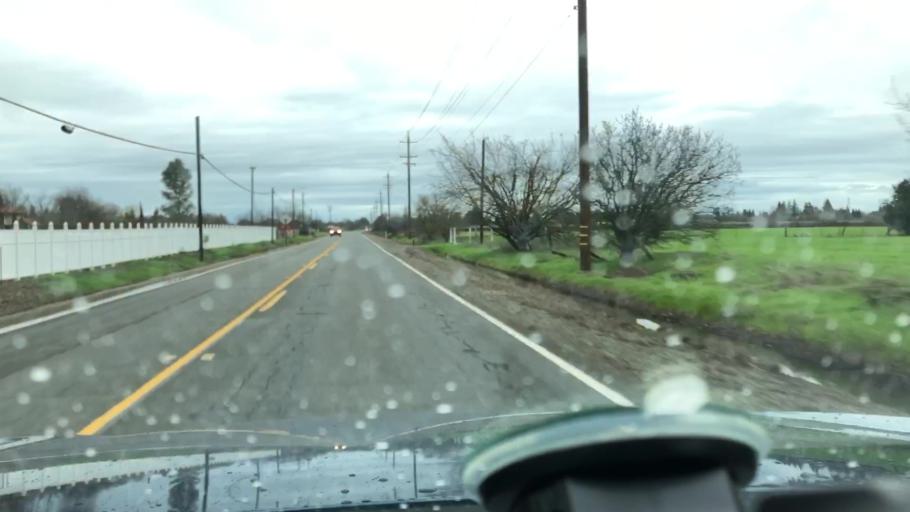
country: US
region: California
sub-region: Sacramento County
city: Wilton
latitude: 38.4139
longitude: -121.3200
